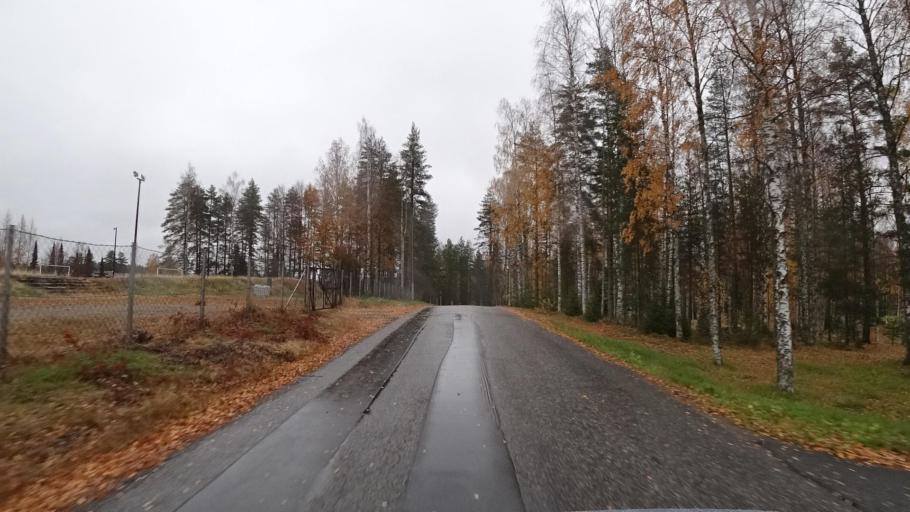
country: FI
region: North Karelia
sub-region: Joensuu
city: Outokumpu
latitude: 62.7320
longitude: 29.0038
